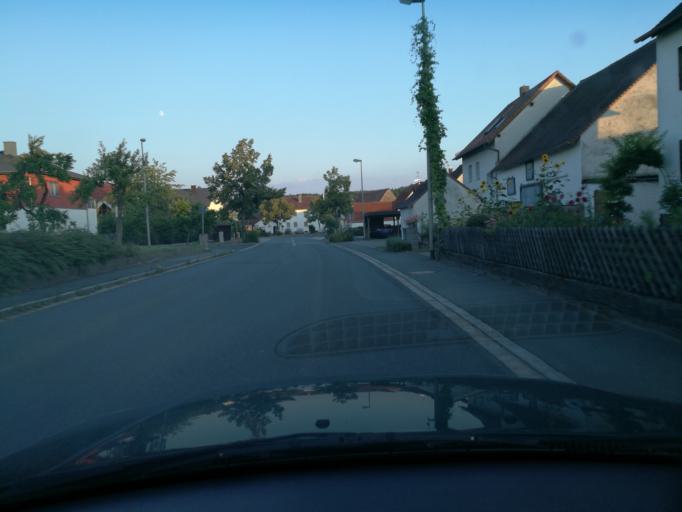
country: DE
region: Bavaria
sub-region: Regierungsbezirk Mittelfranken
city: Hessdorf
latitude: 49.6167
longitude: 10.9082
